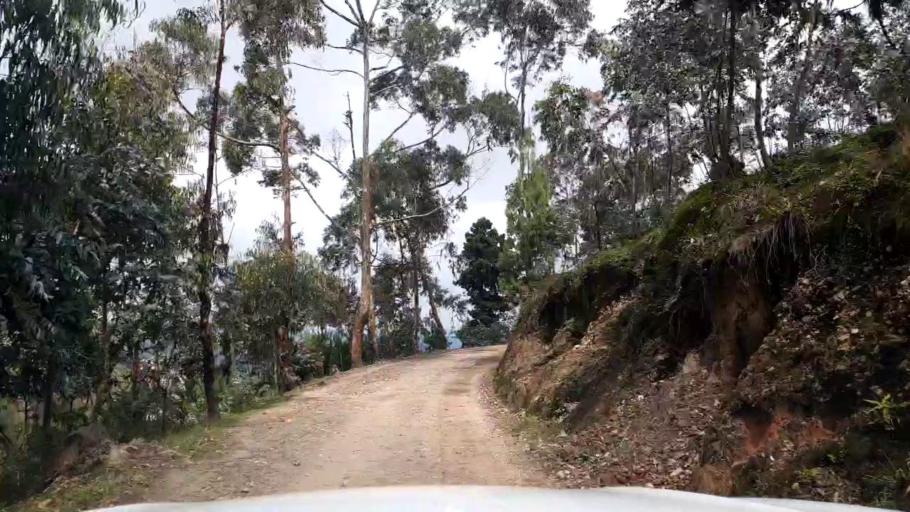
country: RW
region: Western Province
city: Kibuye
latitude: -1.9388
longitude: 29.4651
